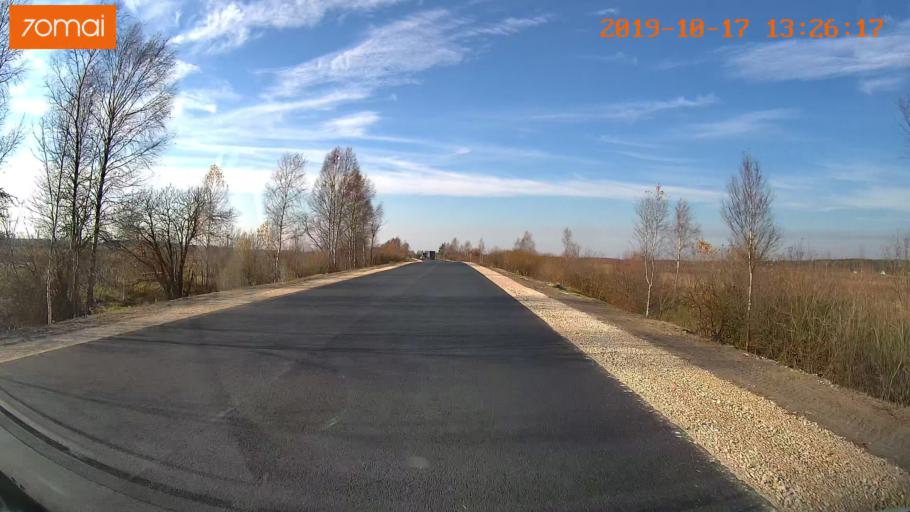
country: RU
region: Rjazan
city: Gus'-Zheleznyy
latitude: 55.1091
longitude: 40.9251
